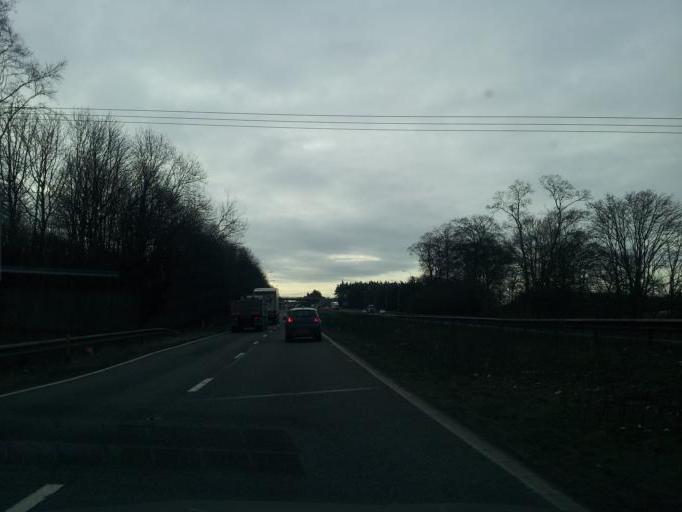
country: GB
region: England
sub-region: Lincolnshire
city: Grantham
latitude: 52.8184
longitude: -0.6235
